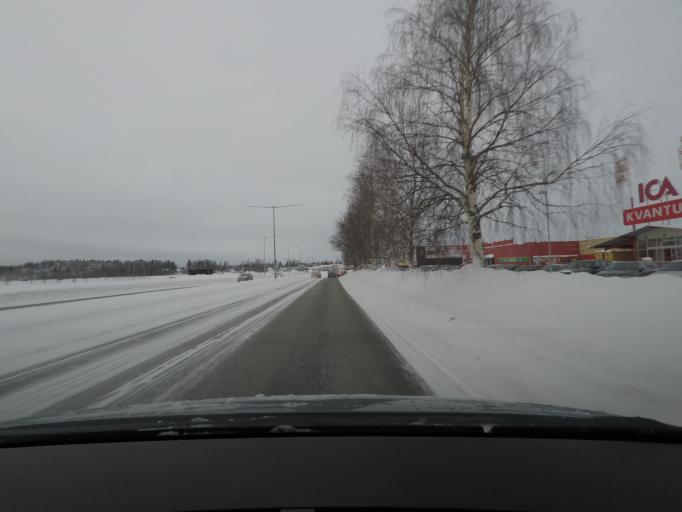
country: SE
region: Norrbotten
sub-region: Lulea Kommun
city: Lulea
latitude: 65.5942
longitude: 22.1495
